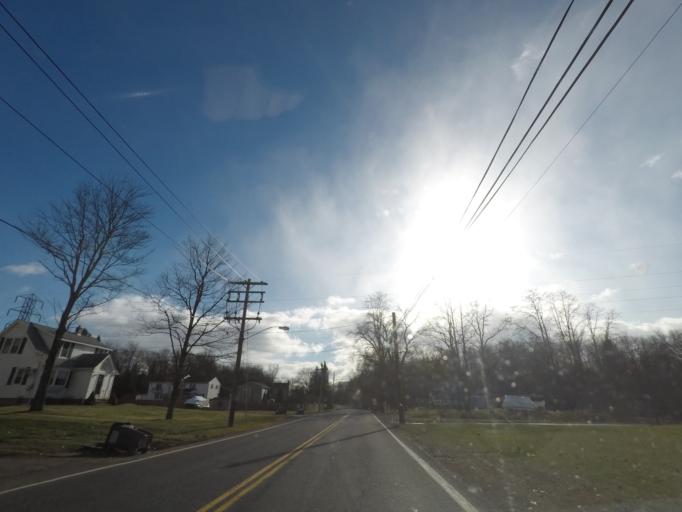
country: US
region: New York
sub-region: Schenectady County
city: Niskayuna
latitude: 42.7436
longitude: -73.8694
